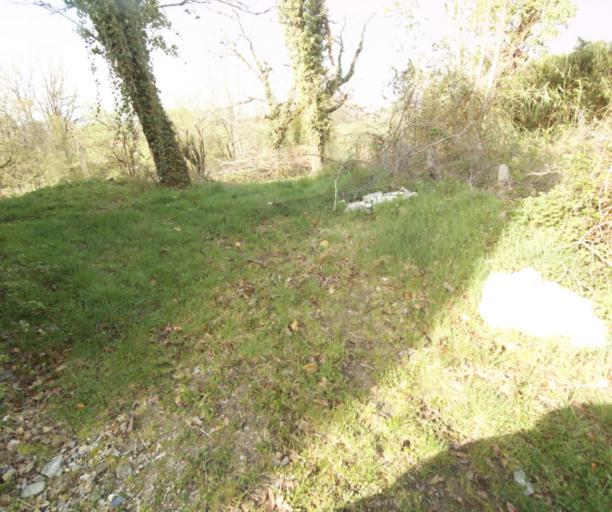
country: FR
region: Limousin
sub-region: Departement de la Correze
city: Correze
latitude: 45.3405
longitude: 1.8366
